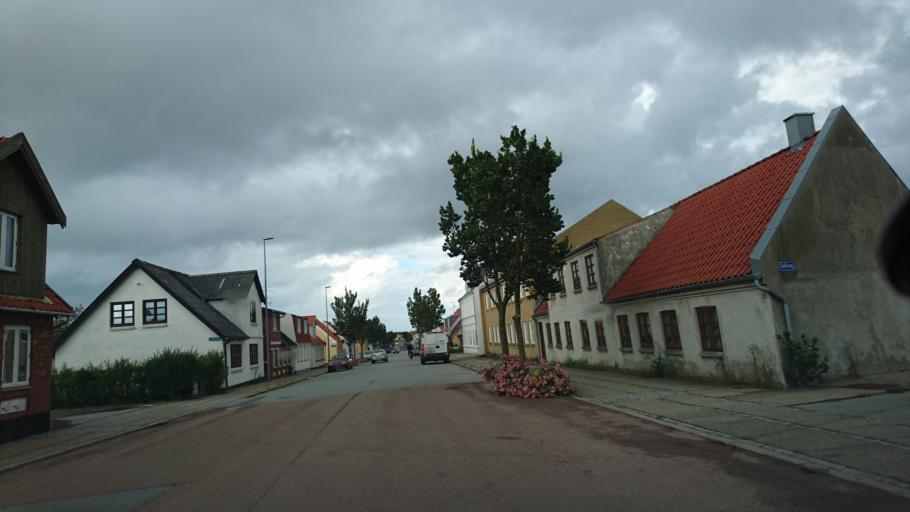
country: DK
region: North Denmark
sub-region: Frederikshavn Kommune
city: Frederikshavn
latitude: 57.4284
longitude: 10.5216
